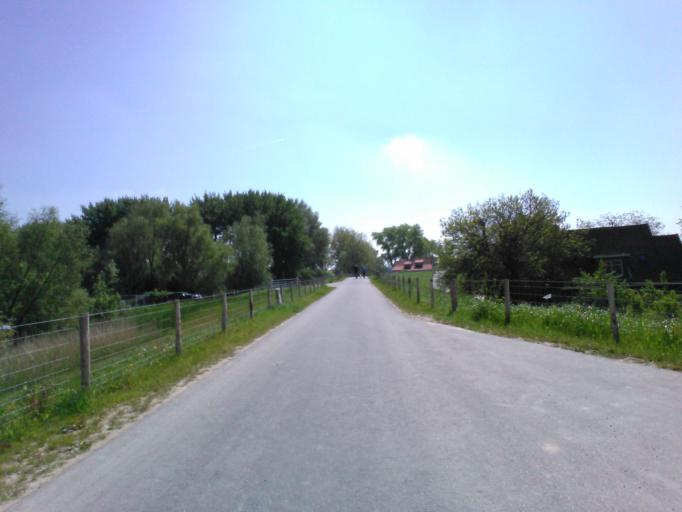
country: NL
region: South Holland
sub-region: Gemeente Sliedrecht
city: Sliedrecht
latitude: 51.7904
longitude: 4.7574
